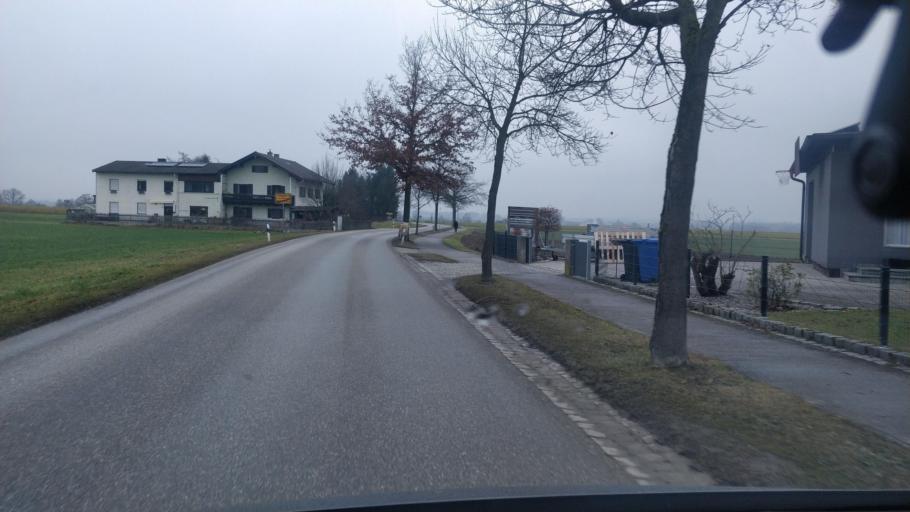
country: DE
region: Bavaria
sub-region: Upper Bavaria
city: Obertaufkirchen
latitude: 48.2638
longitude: 12.2763
